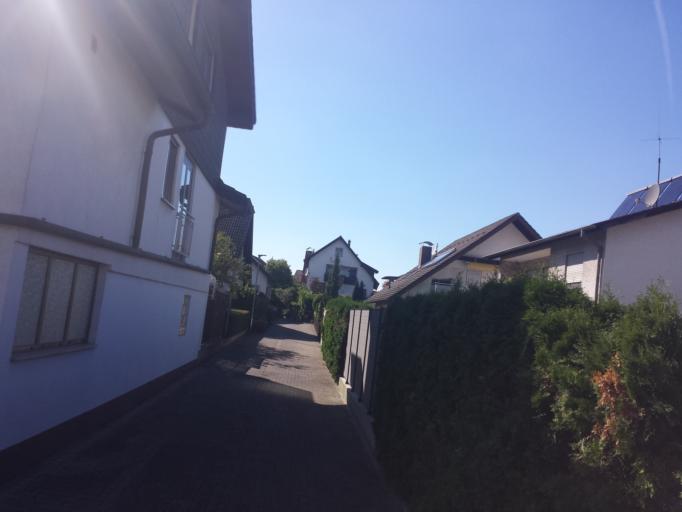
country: DE
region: Hesse
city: Lorsch
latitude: 49.6578
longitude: 8.5707
